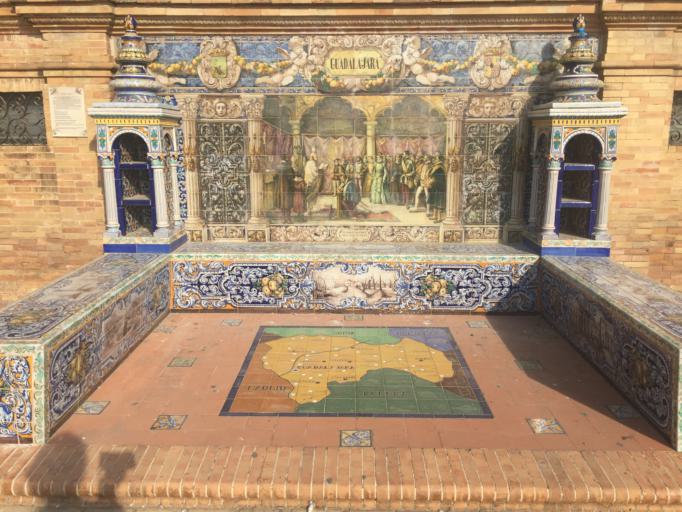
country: ES
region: Andalusia
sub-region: Provincia de Sevilla
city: Sevilla
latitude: 37.3779
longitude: -5.9865
